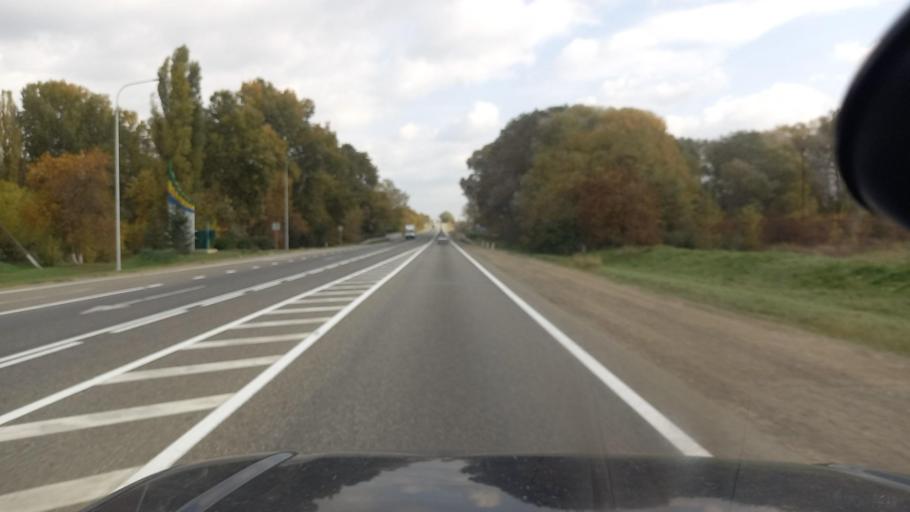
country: RU
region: Krasnodarskiy
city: Chernomorskiy
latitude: 44.8532
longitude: 38.4498
